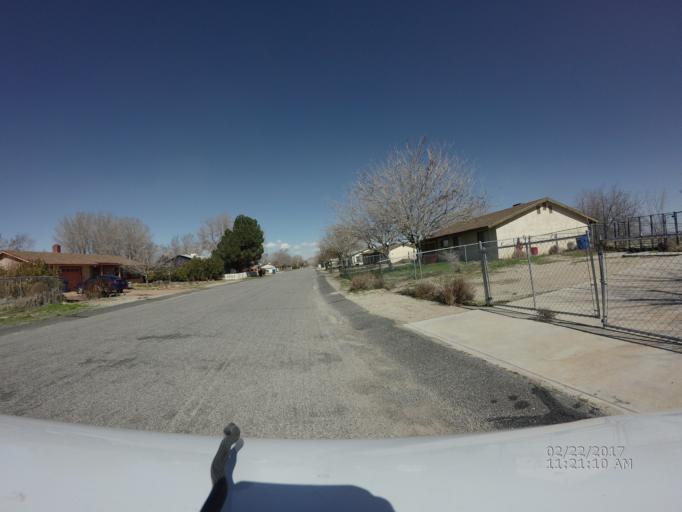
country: US
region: California
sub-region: Los Angeles County
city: Lake Los Angeles
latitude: 34.6178
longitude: -117.8105
